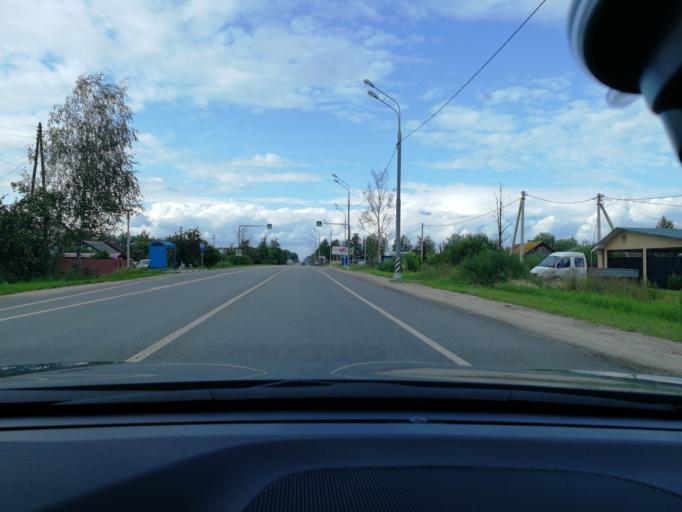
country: RU
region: Moskovskaya
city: Proletarskiy
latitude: 55.0349
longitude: 37.4291
